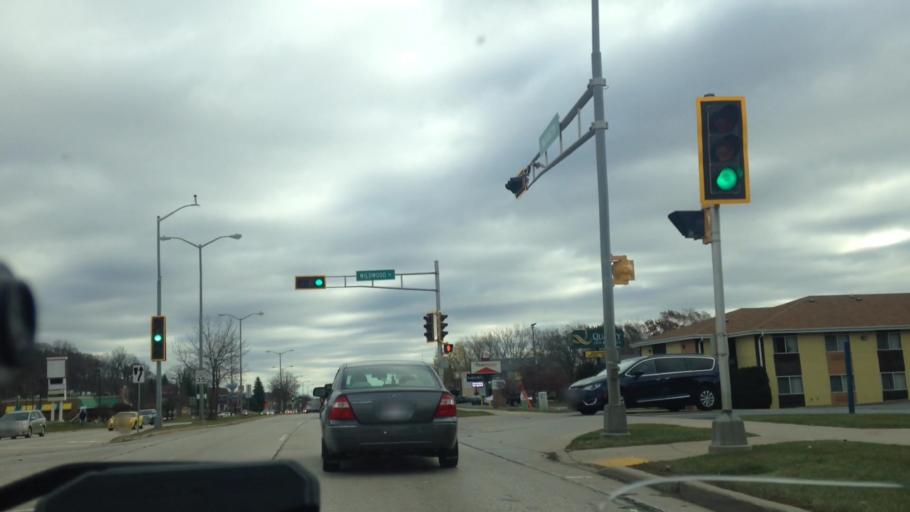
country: US
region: Wisconsin
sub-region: Washington County
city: West Bend
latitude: 43.4272
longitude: -88.2164
